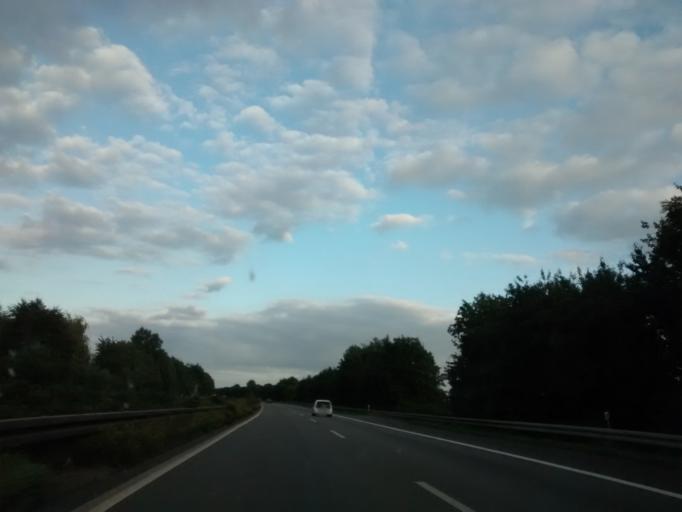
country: DE
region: North Rhine-Westphalia
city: Ibbenburen
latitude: 52.2569
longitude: 7.7163
